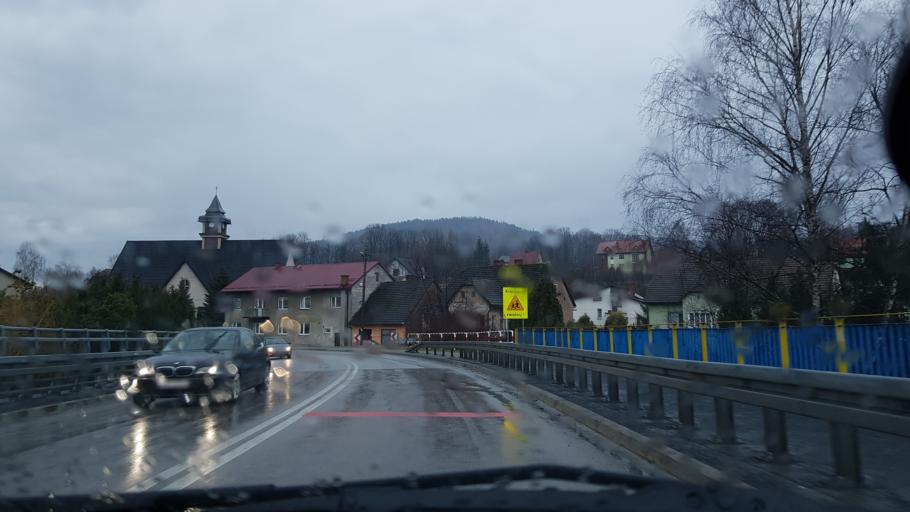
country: PL
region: Lesser Poland Voivodeship
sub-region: Powiat suski
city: Stryszawa
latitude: 49.7349
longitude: 19.5312
